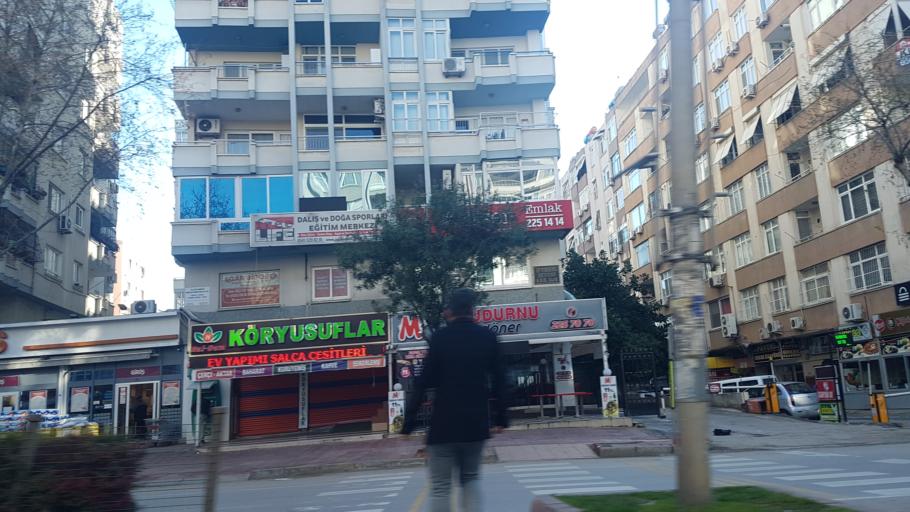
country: TR
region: Adana
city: Adana
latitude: 37.0243
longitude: 35.3148
